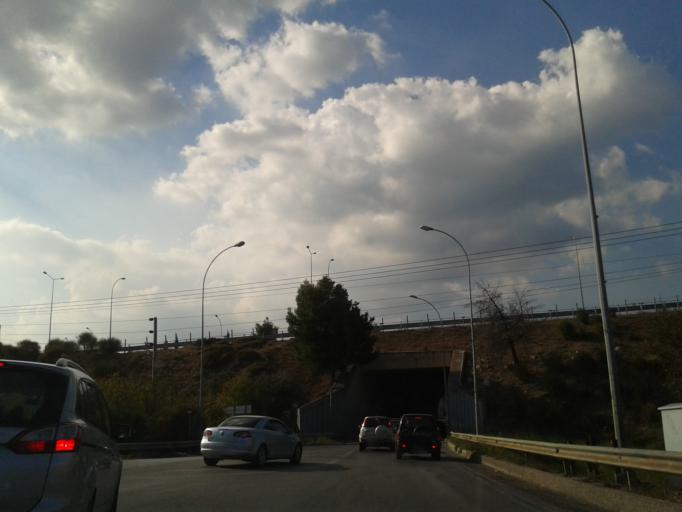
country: GR
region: Attica
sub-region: Nomarchia Anatolikis Attikis
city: Agios Stefanos
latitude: 38.1395
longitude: 23.8446
